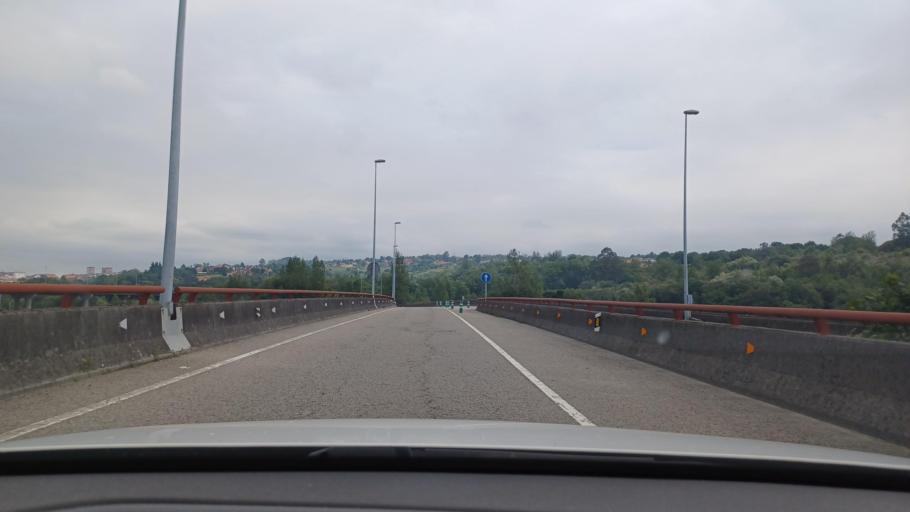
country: ES
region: Asturias
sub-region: Province of Asturias
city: Oviedo
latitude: 43.3438
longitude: -5.8660
